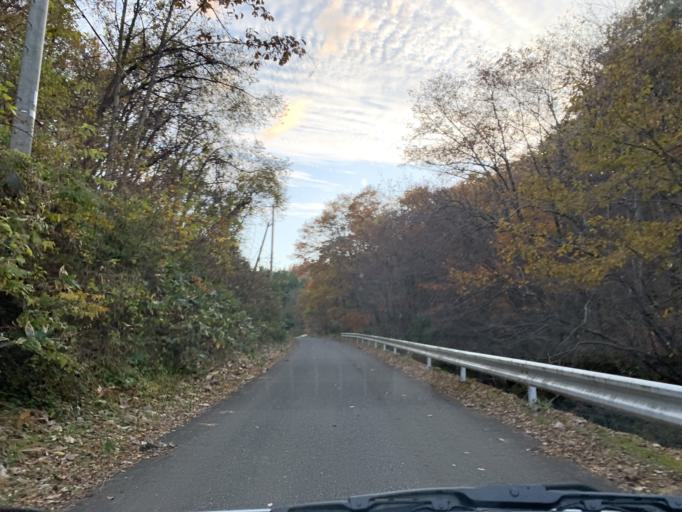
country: JP
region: Iwate
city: Ichinoseki
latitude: 39.0012
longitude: 141.0060
